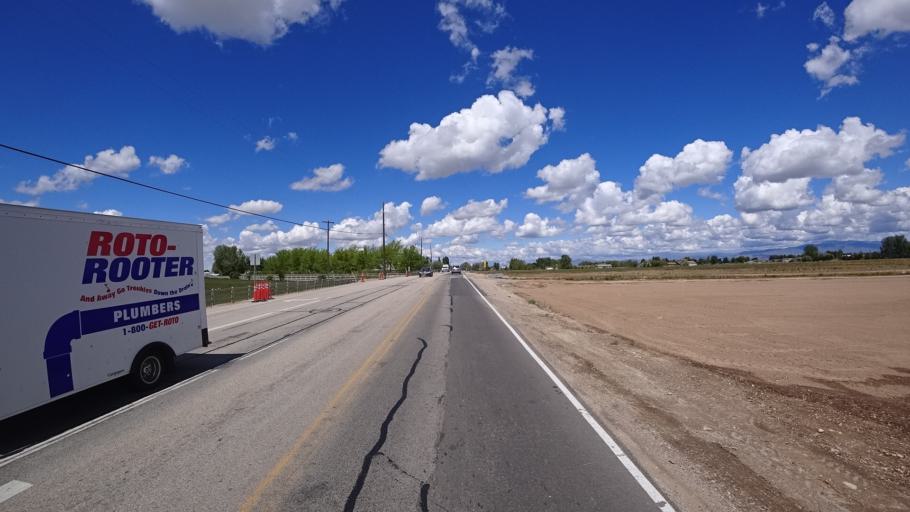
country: US
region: Idaho
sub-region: Ada County
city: Meridian
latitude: 43.5759
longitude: -116.4337
